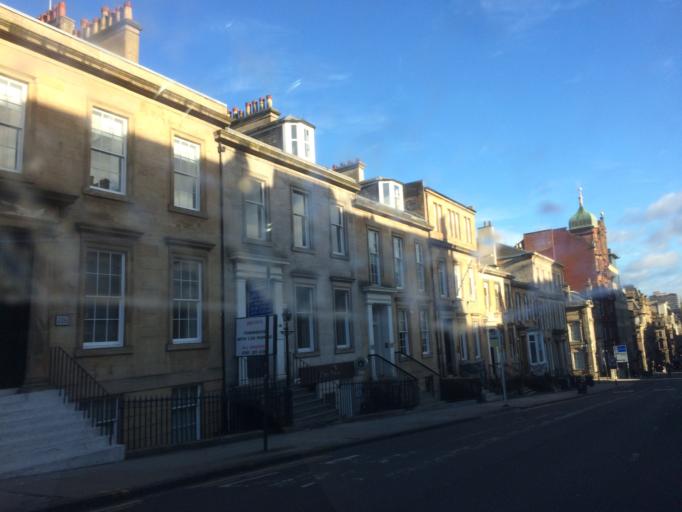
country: GB
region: Scotland
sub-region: Glasgow City
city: Glasgow
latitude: 55.8628
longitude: -4.2609
